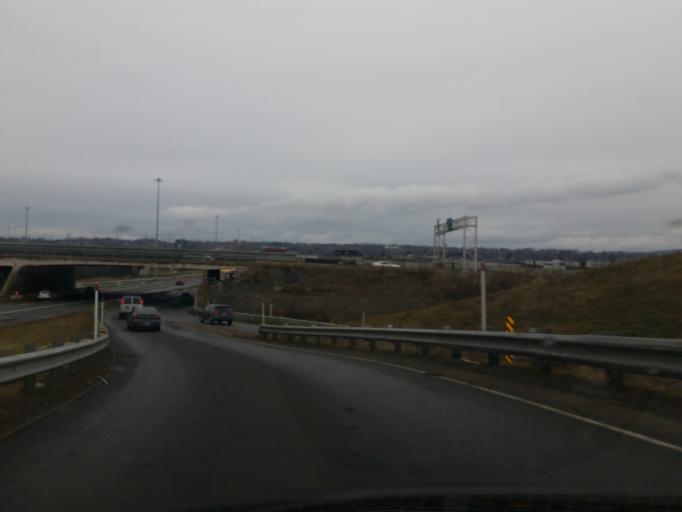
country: CA
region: Quebec
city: Quebec
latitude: 46.8363
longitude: -71.2628
